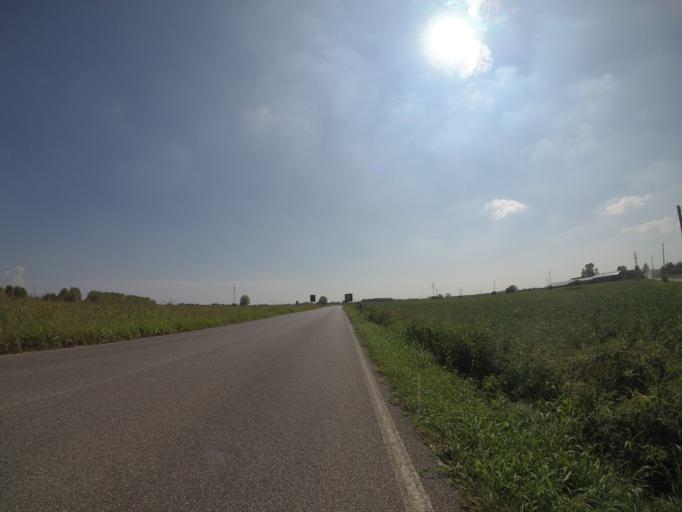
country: IT
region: Friuli Venezia Giulia
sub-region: Provincia di Udine
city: Pocenia
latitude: 45.8214
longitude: 13.1011
